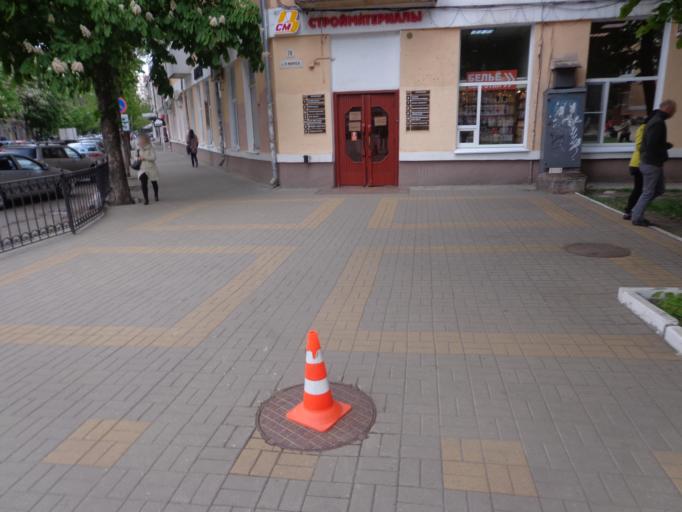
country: RU
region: Voronezj
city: Voronezh
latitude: 51.6663
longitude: 39.2027
